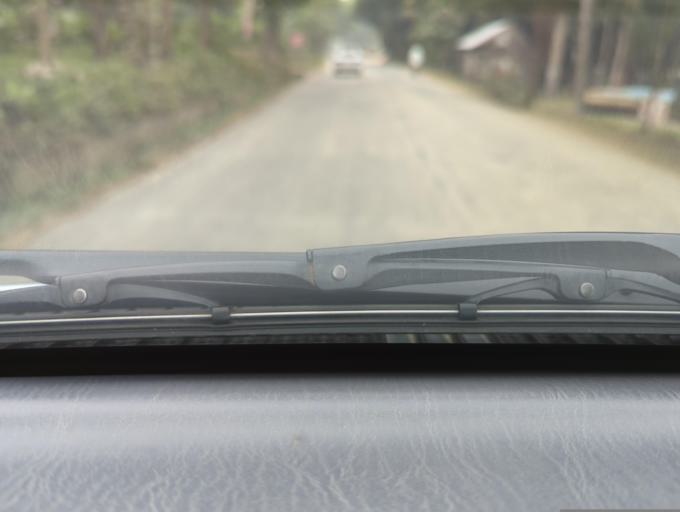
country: BD
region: Sylhet
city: Maulavi Bazar
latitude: 24.5166
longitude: 91.7284
